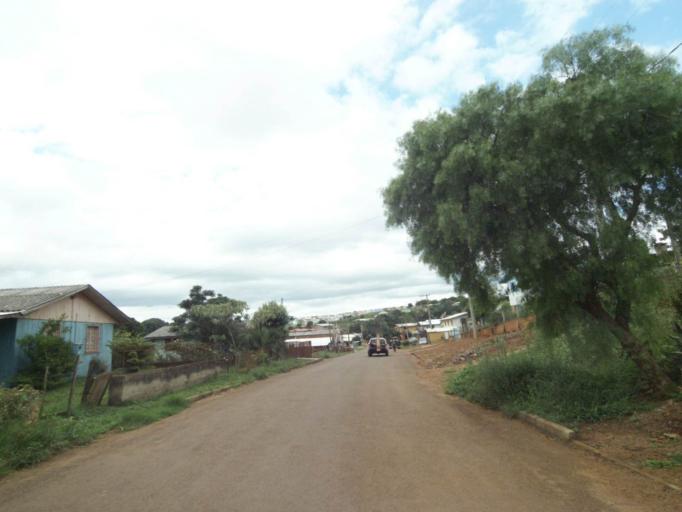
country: BR
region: Rio Grande do Sul
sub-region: Lagoa Vermelha
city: Lagoa Vermelha
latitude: -28.1991
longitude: -51.5287
